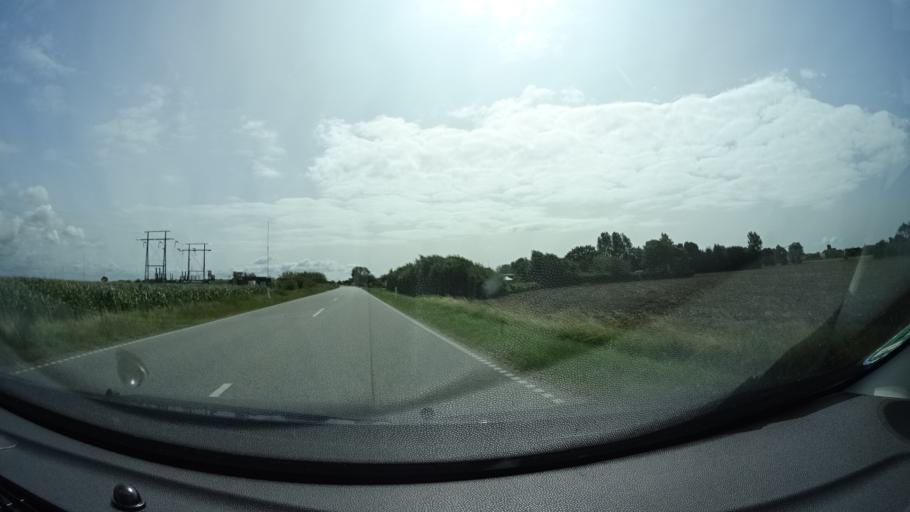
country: DE
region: Schleswig-Holstein
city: Rodenas
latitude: 54.9678
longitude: 8.7014
